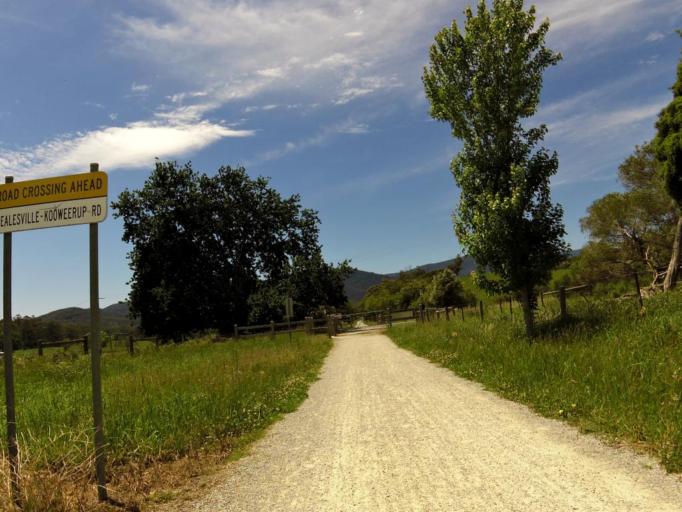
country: AU
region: Victoria
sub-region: Yarra Ranges
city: Woori Yallock
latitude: -37.7728
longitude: 145.5375
